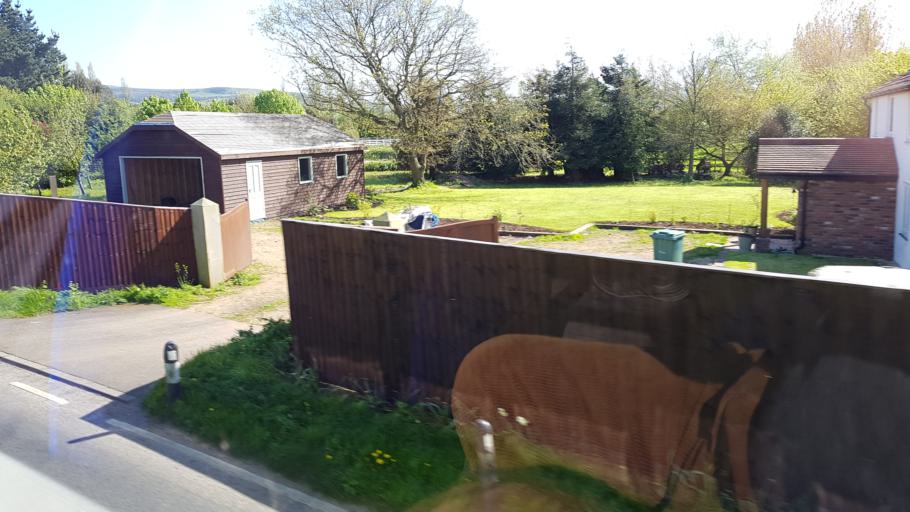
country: GB
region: England
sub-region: Isle of Wight
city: Newchurch
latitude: 50.6512
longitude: -1.2181
